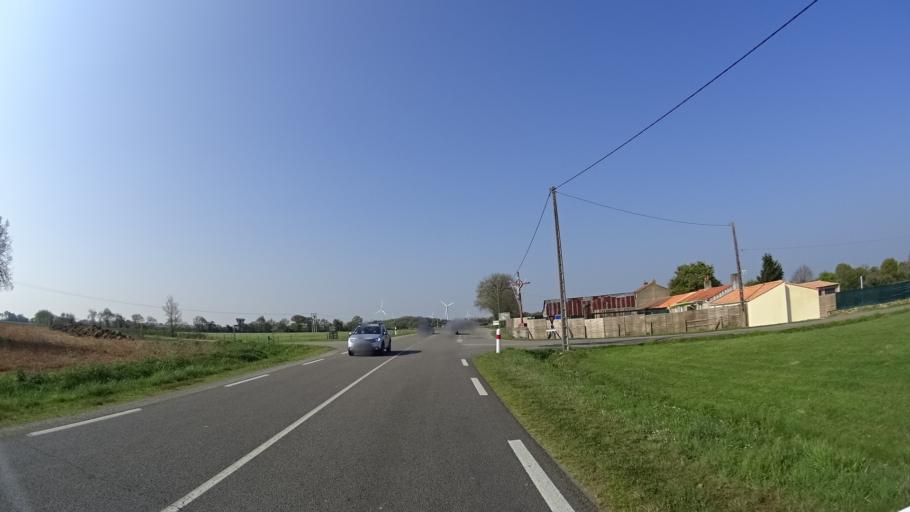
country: FR
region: Pays de la Loire
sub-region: Departement de la Loire-Atlantique
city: Saint-Hilaire-de-Chaleons
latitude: 47.0834
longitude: -1.8605
